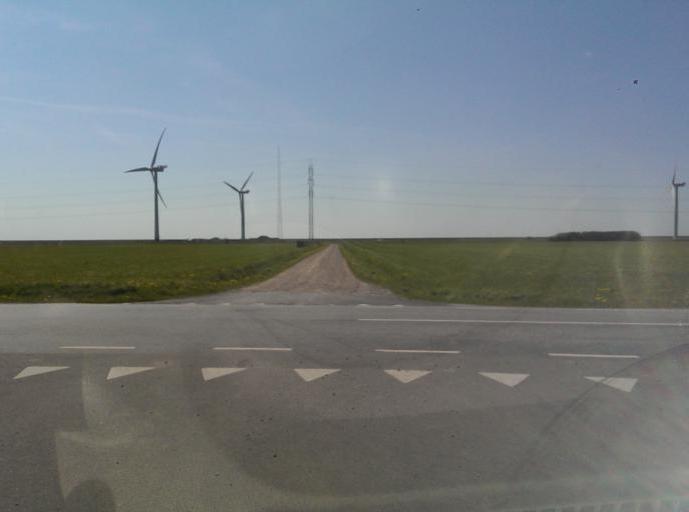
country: DK
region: South Denmark
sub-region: Esbjerg Kommune
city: Tjaereborg
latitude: 55.4535
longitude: 8.5932
